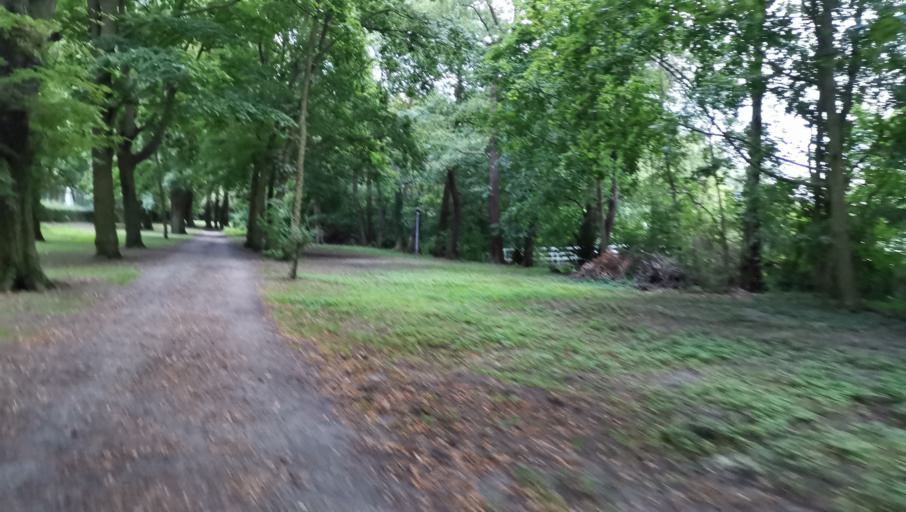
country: DE
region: Brandenburg
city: Potsdam
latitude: 52.3825
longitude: 13.0307
